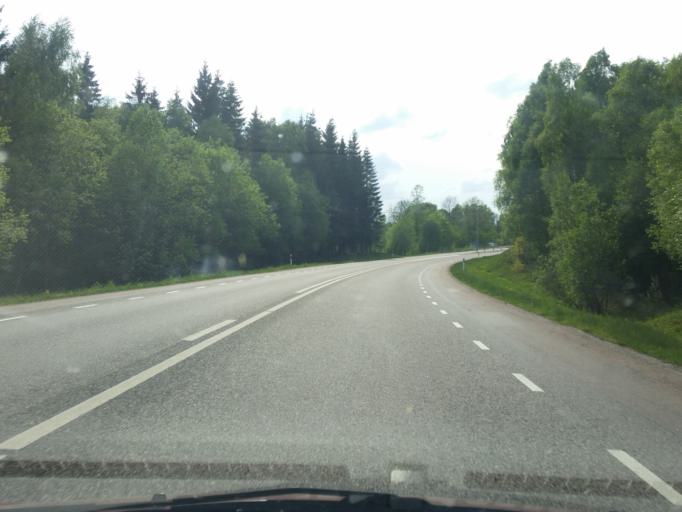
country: SE
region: Vaestra Goetaland
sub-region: Ulricehamns Kommun
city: Ulricehamn
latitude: 57.8033
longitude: 13.3064
